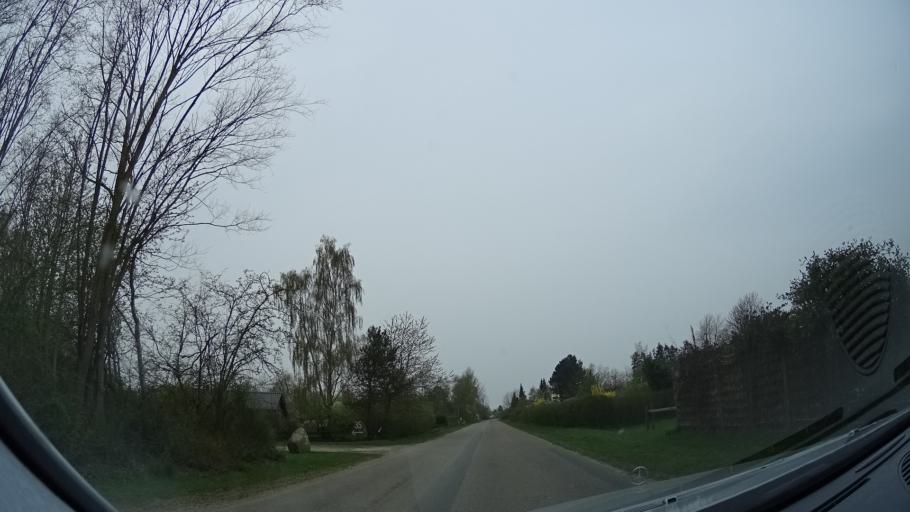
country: DK
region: Zealand
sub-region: Lejre Kommune
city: Ejby
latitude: 55.7077
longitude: 11.8501
